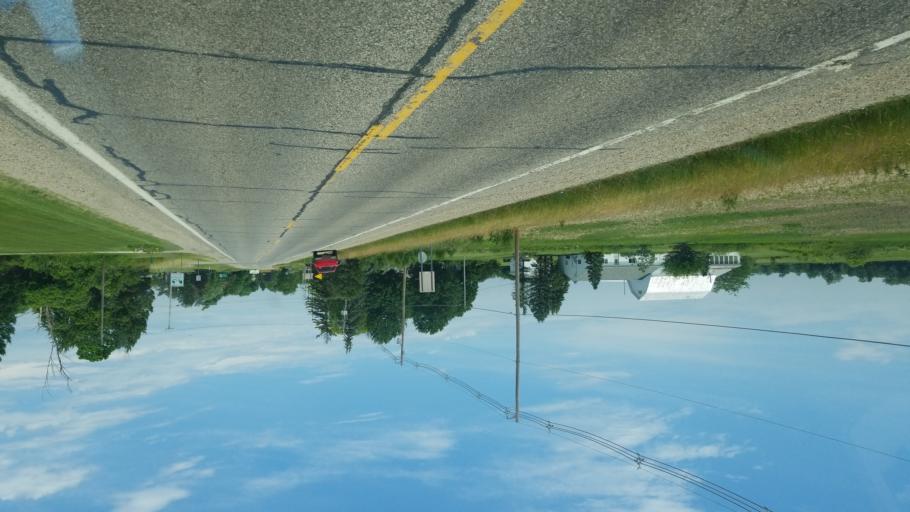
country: US
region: Michigan
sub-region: Eaton County
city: Charlotte
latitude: 42.5656
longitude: -84.8541
